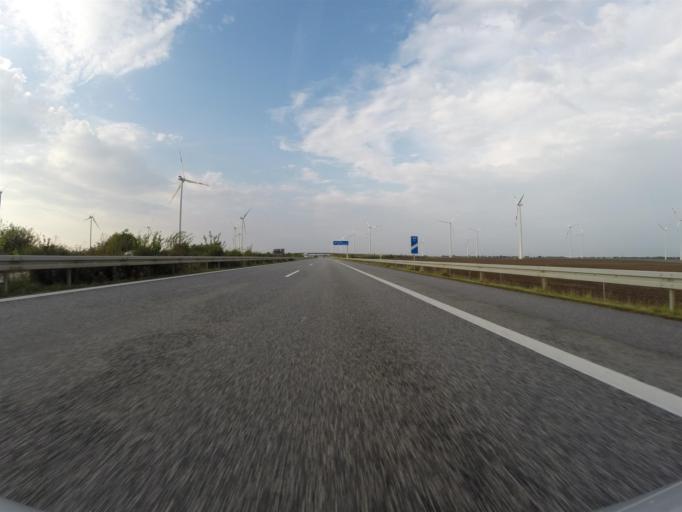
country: DE
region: Saxony-Anhalt
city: Bad Lauchstadt
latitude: 51.4212
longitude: 11.8634
